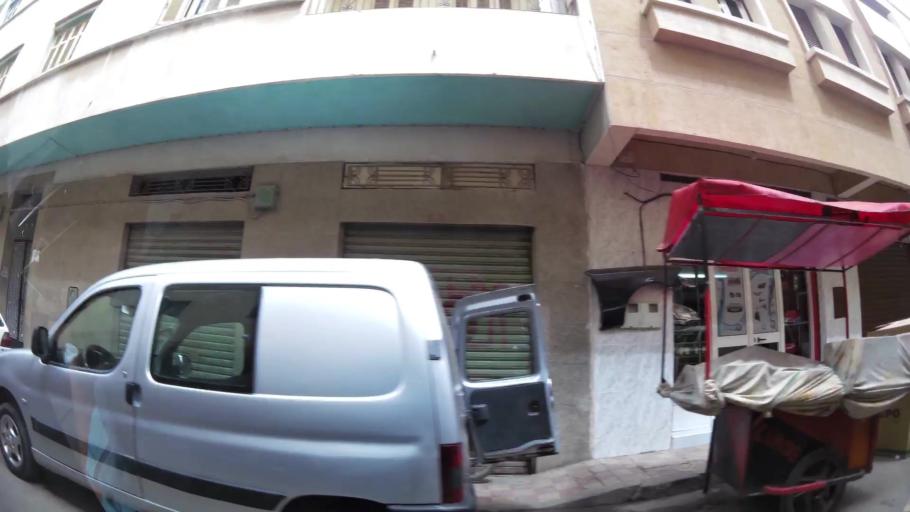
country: MA
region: Oriental
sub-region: Nador
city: Nador
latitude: 35.1777
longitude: -2.9287
